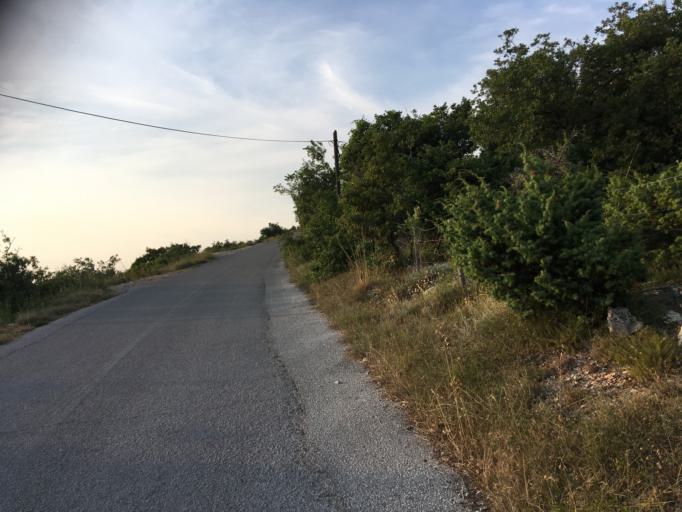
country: HR
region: Primorsko-Goranska
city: Punat
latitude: 44.9920
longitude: 14.6314
